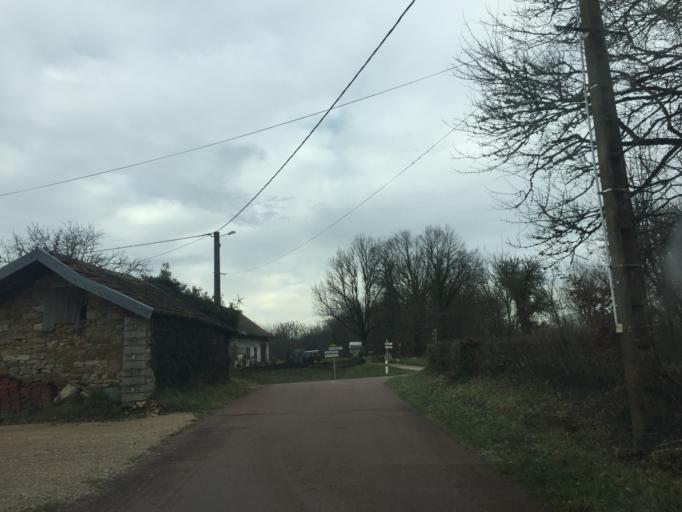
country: FR
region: Franche-Comte
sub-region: Departement du Jura
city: Mont-sous-Vaudrey
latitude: 46.8700
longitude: 5.5393
